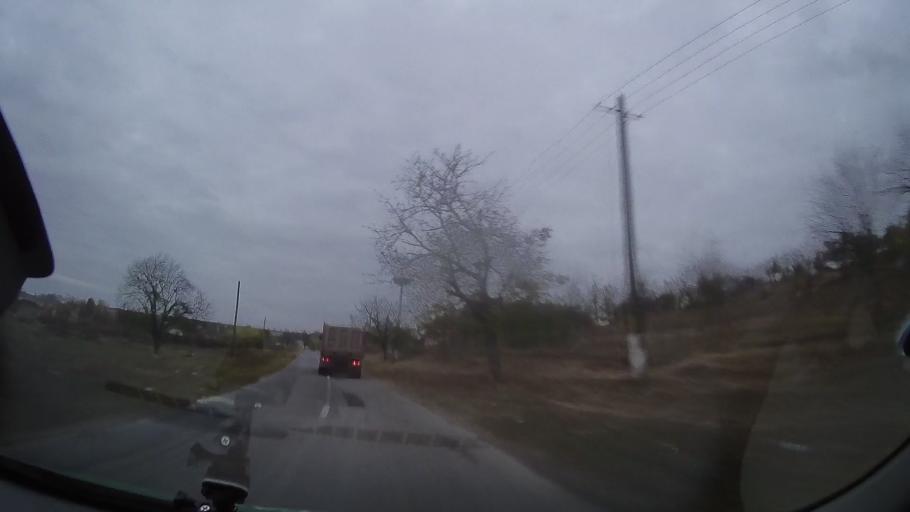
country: RO
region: Tulcea
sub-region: Comuna Mihai Bravu
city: Mihai Bravu
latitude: 44.9568
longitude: 28.6501
